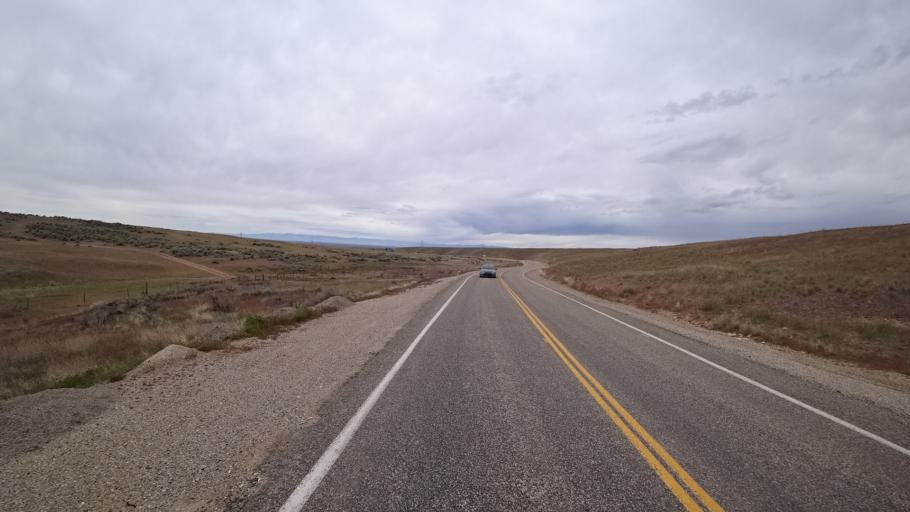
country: US
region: Idaho
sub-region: Ada County
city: Boise
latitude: 43.4762
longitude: -116.0501
